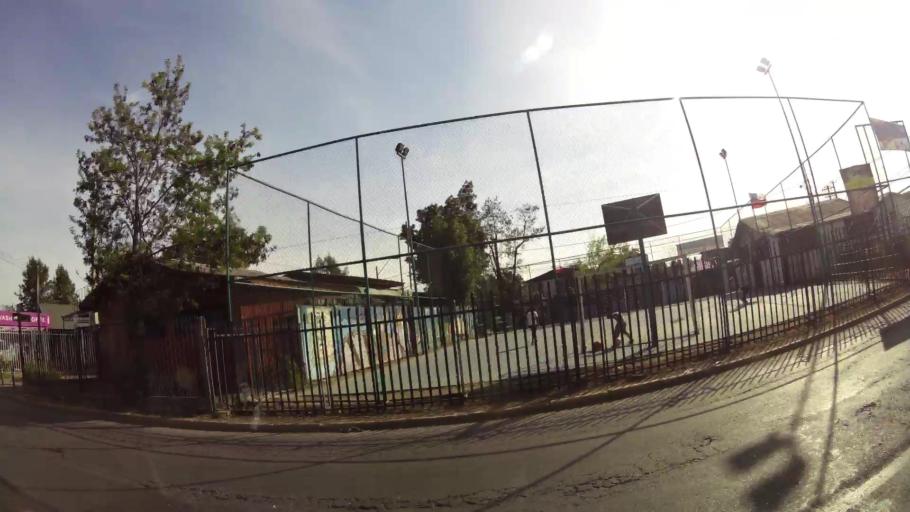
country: CL
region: Santiago Metropolitan
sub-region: Provincia de Santiago
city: La Pintana
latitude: -33.5305
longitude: -70.5900
